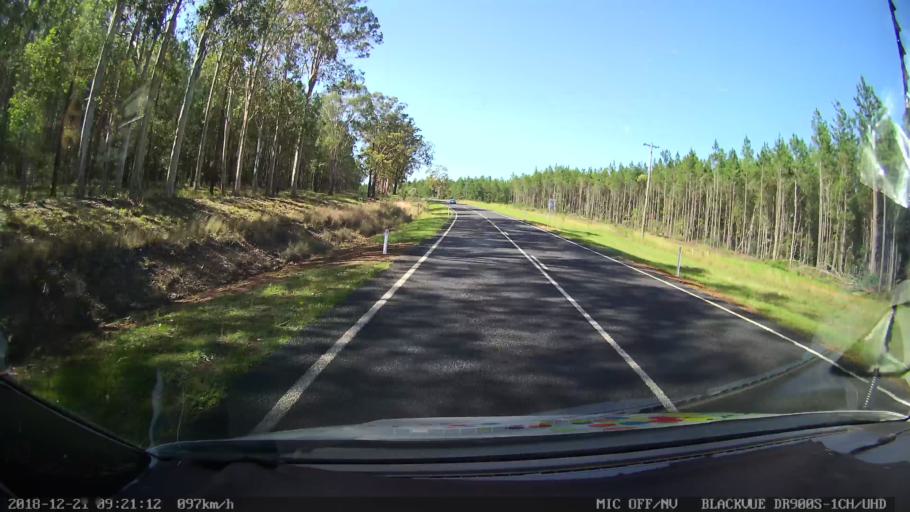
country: AU
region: New South Wales
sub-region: Clarence Valley
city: Maclean
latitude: -29.3257
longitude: 152.9978
